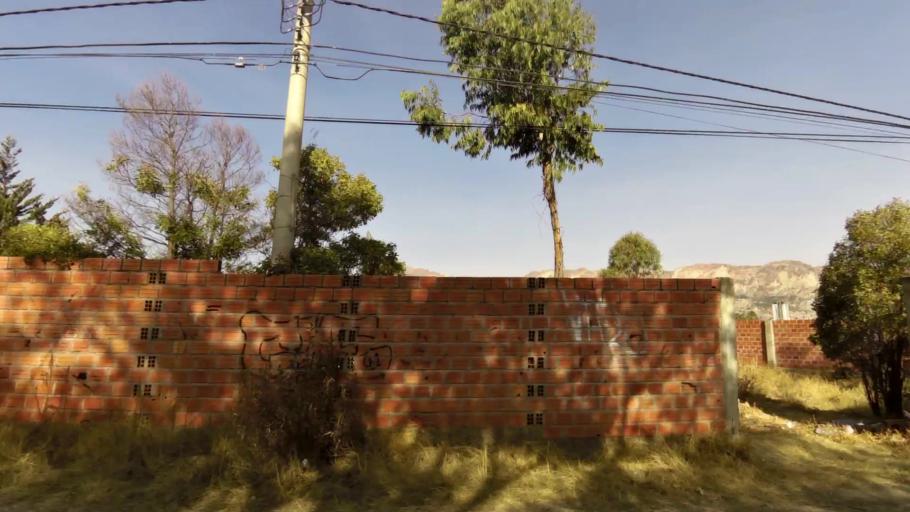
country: BO
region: La Paz
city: La Paz
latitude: -16.5293
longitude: -68.0796
